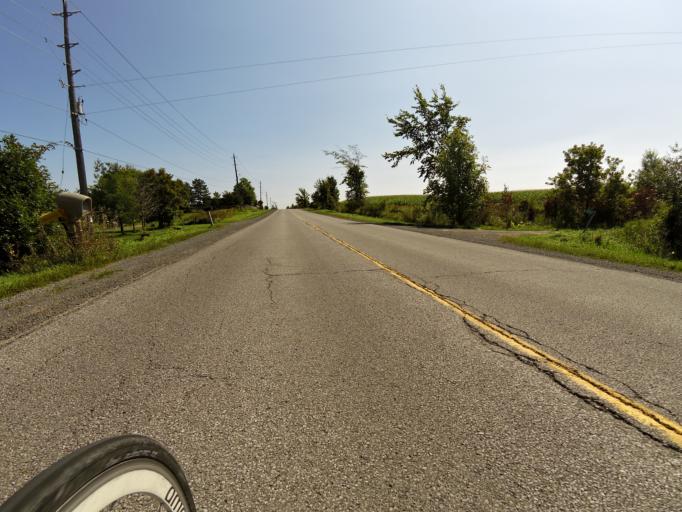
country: CA
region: Ontario
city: Arnprior
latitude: 45.4604
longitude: -76.0971
